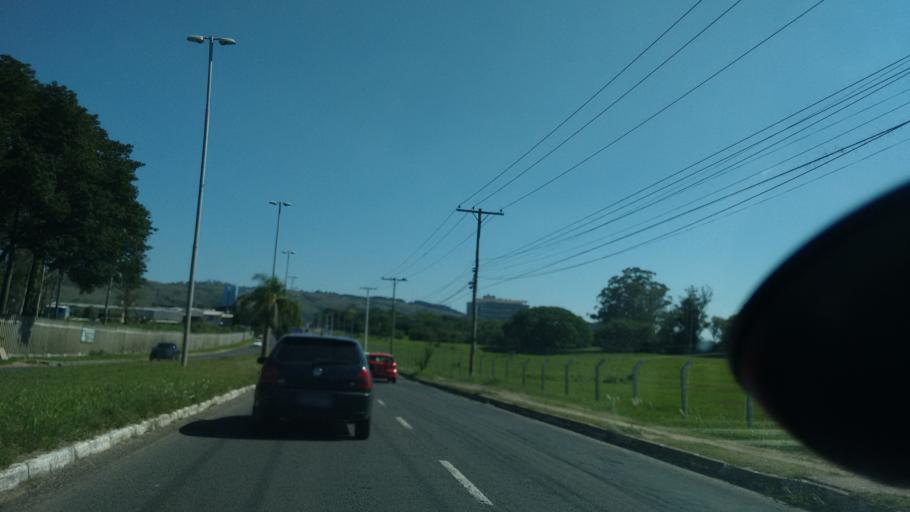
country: BR
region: Rio Grande do Sul
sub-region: Cachoeirinha
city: Cachoeirinha
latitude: -30.0277
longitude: -51.1204
